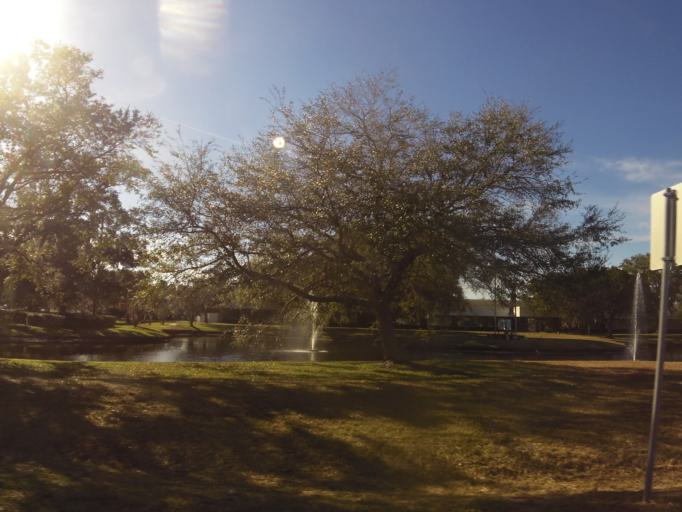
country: US
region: Florida
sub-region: Saint Johns County
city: Saint Augustine
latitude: 29.9203
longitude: -81.4033
